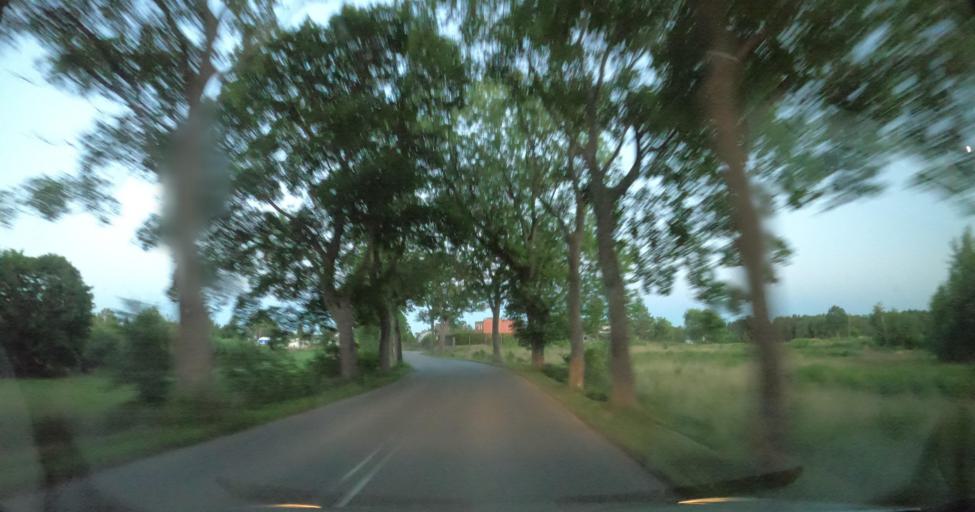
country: PL
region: Pomeranian Voivodeship
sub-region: Powiat wejherowski
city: Szemud
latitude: 54.4721
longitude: 18.2746
